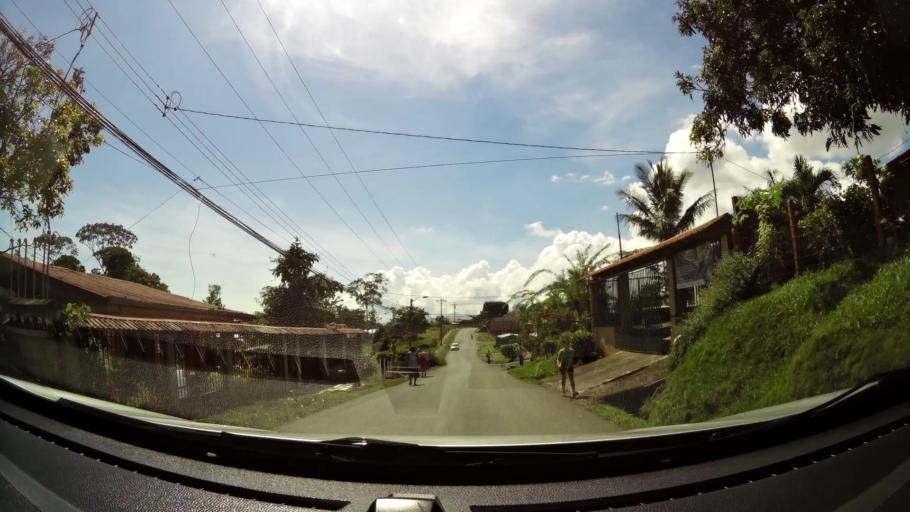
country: CR
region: San Jose
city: San Isidro
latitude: 9.3820
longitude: -83.6975
